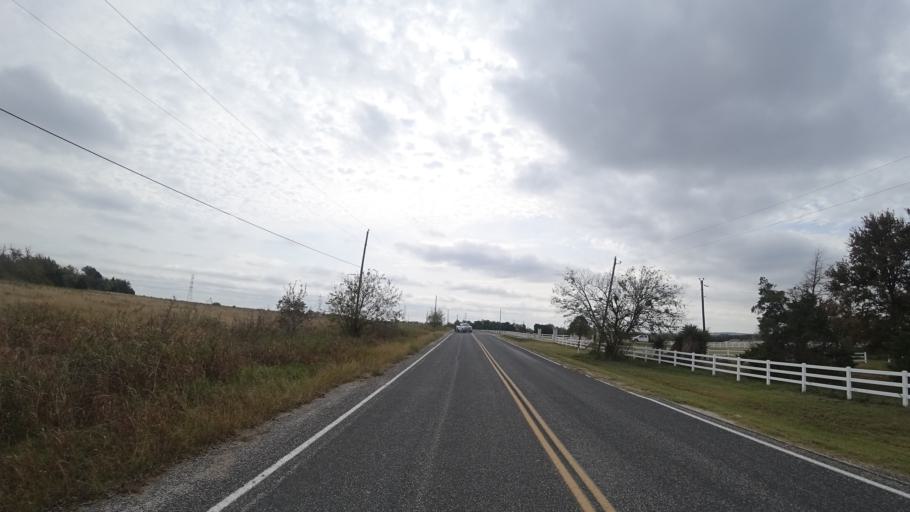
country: US
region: Texas
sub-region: Travis County
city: Manor
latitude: 30.3800
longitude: -97.5845
